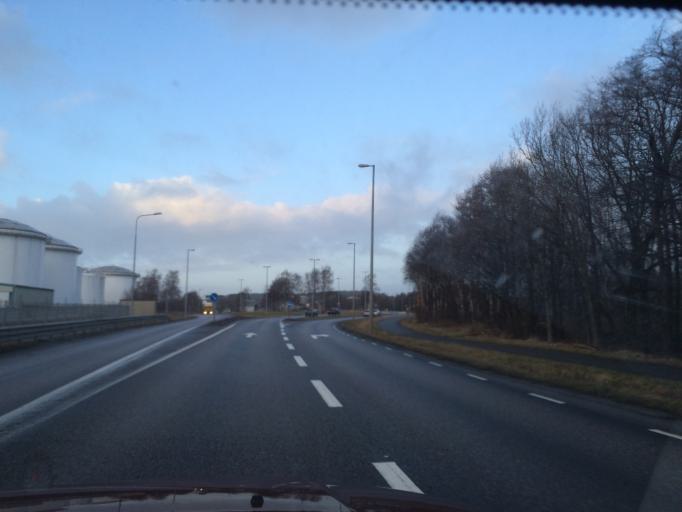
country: SE
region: Vaestra Goetaland
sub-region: Goteborg
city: Majorna
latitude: 57.6990
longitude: 11.8734
